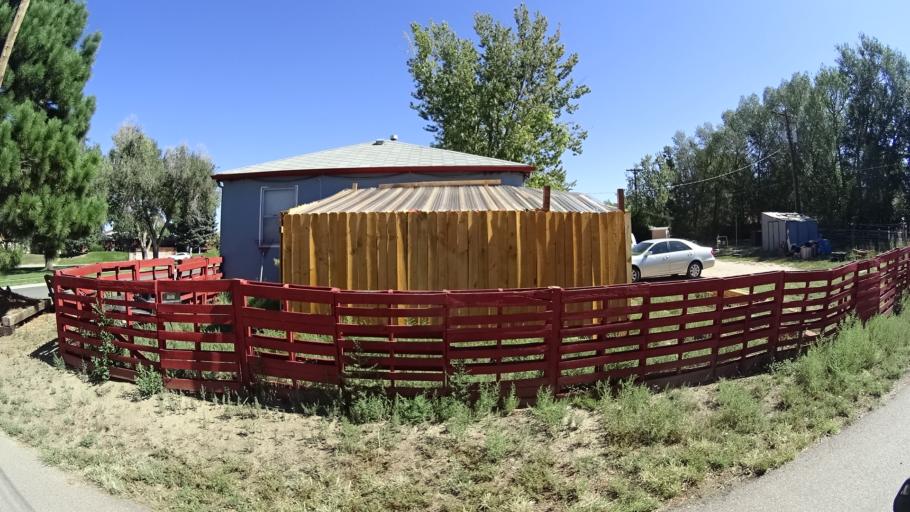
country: US
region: Colorado
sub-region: El Paso County
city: Colorado Springs
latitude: 38.8536
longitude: -104.8003
